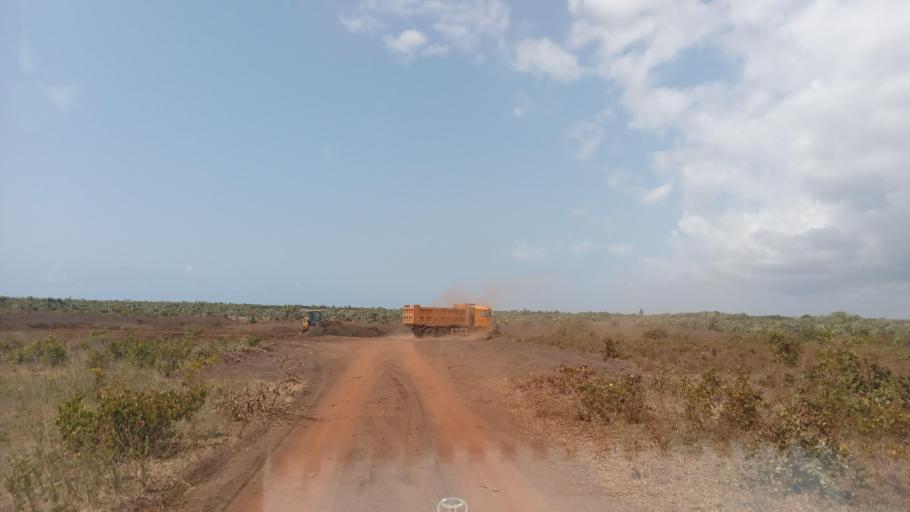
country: MG
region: Atsimo-Atsinanana
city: Vohipaho
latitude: -23.8520
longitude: 47.5507
